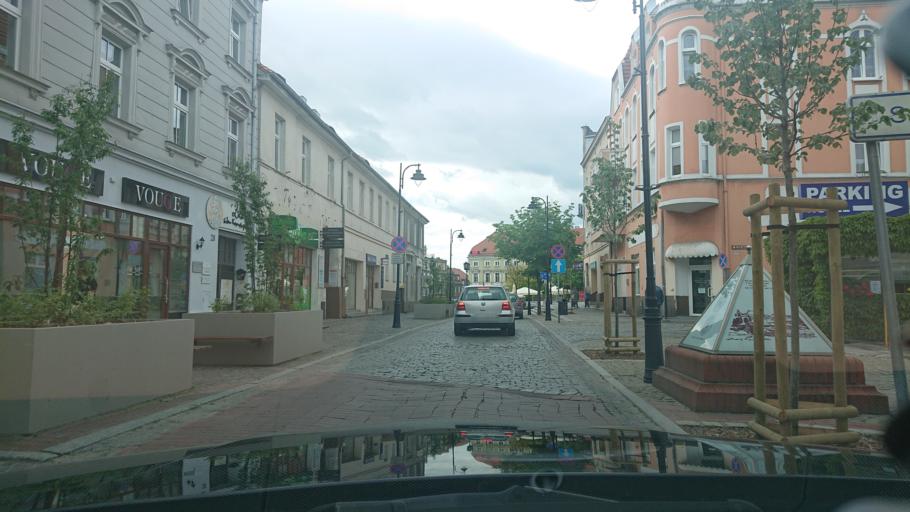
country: PL
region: Greater Poland Voivodeship
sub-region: Powiat gnieznienski
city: Gniezno
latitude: 52.5361
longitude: 17.5976
